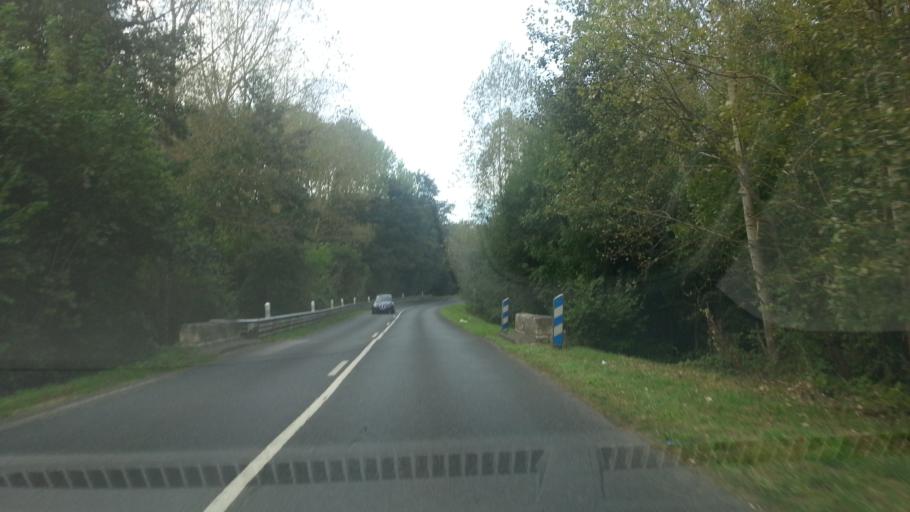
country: FR
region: Picardie
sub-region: Departement de l'Oise
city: Senlis
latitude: 49.2089
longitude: 2.5654
